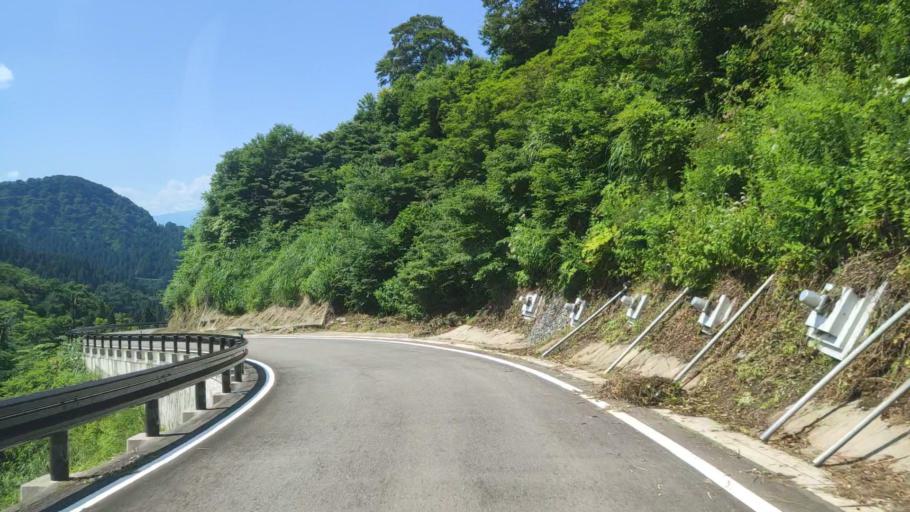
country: JP
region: Fukui
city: Katsuyama
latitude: 36.1478
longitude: 136.5216
